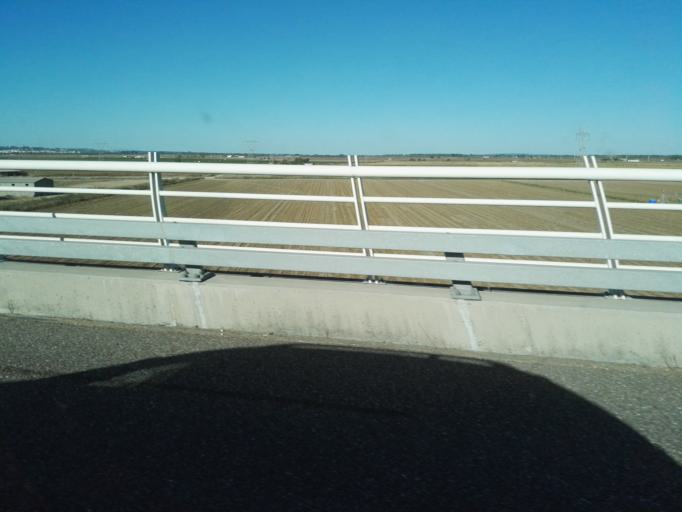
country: PT
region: Santarem
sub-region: Benavente
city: Samora Correia
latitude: 38.9901
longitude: -8.8941
